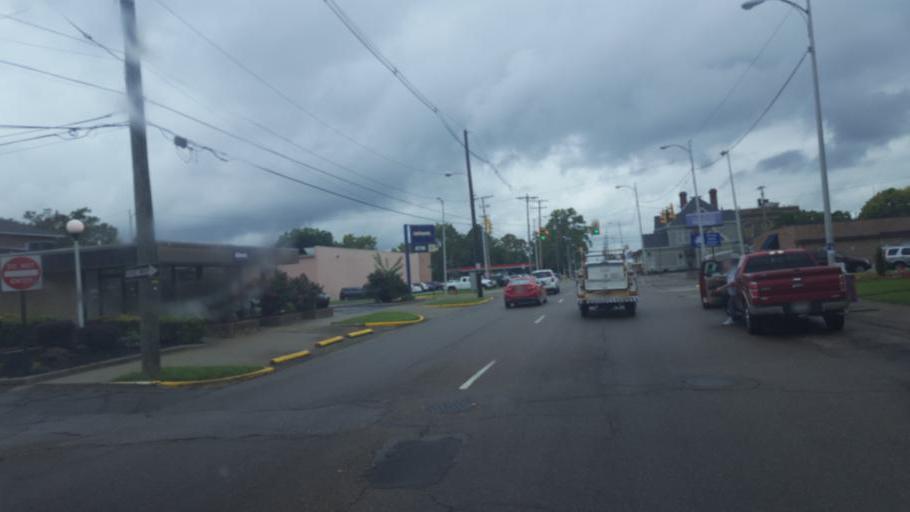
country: US
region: Ohio
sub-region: Scioto County
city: Portsmouth
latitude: 38.7350
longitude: -82.9945
